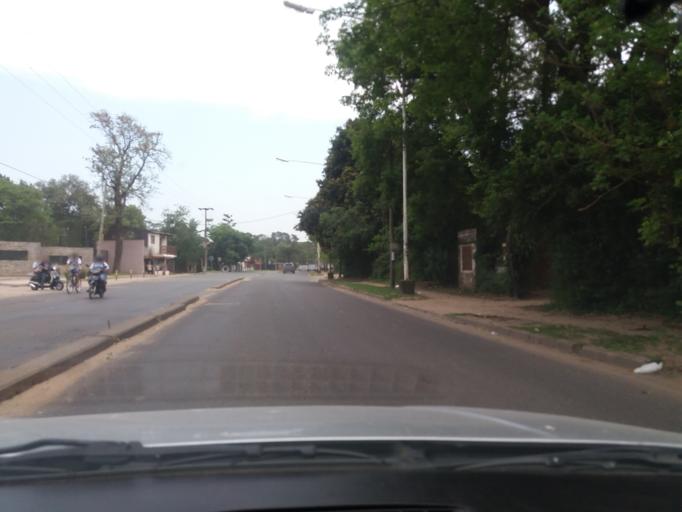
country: AR
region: Corrientes
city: Corrientes
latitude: -27.5103
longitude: -58.8099
